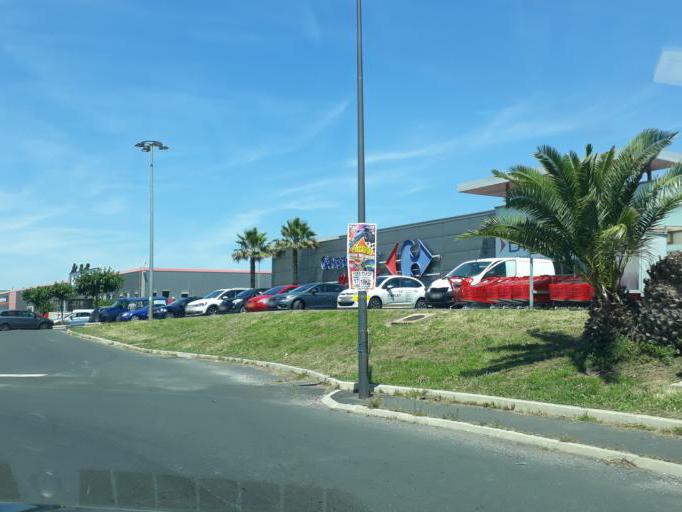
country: FR
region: Languedoc-Roussillon
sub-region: Departement de l'Herault
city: Villeneuve-les-Beziers
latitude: 43.3221
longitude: 3.2901
